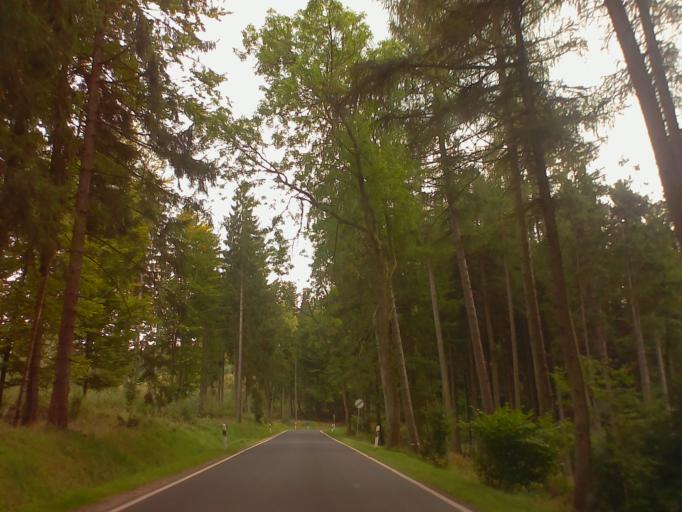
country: DE
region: Thuringia
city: Grossensee
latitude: 50.9254
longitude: 9.9176
